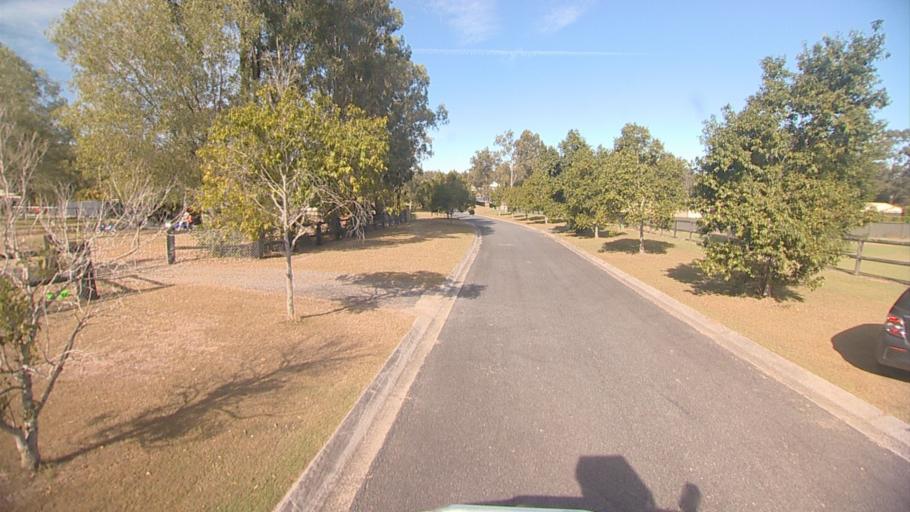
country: AU
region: Queensland
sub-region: Logan
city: North Maclean
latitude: -27.8118
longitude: 152.9624
